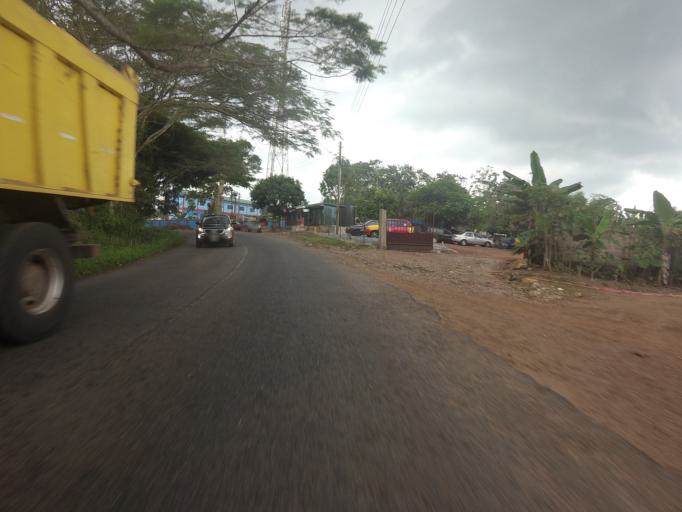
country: GH
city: Akropong
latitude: 5.9429
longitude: -0.1198
